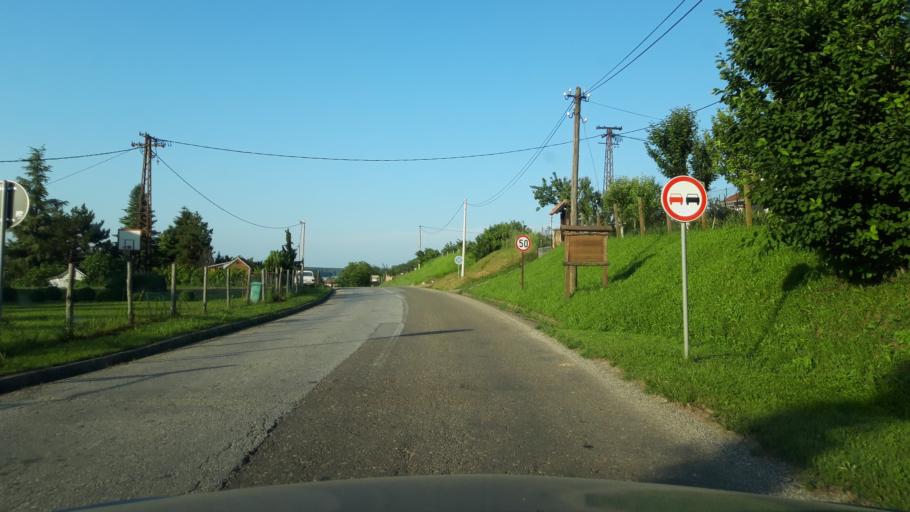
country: RS
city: Glozan
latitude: 45.2097
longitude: 19.6026
